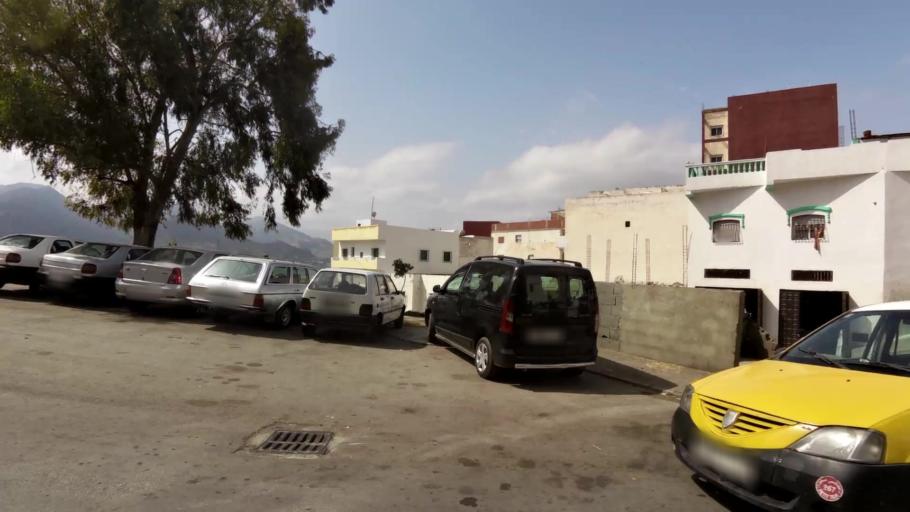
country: MA
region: Tanger-Tetouan
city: Tetouan
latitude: 35.5790
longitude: -5.3865
